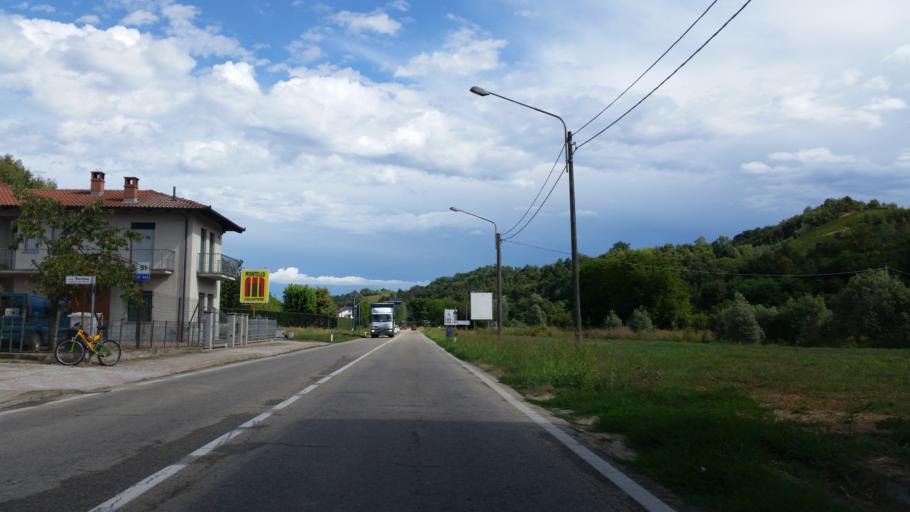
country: IT
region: Piedmont
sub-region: Provincia di Cuneo
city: Vezza d'Alba
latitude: 44.7652
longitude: 8.0090
